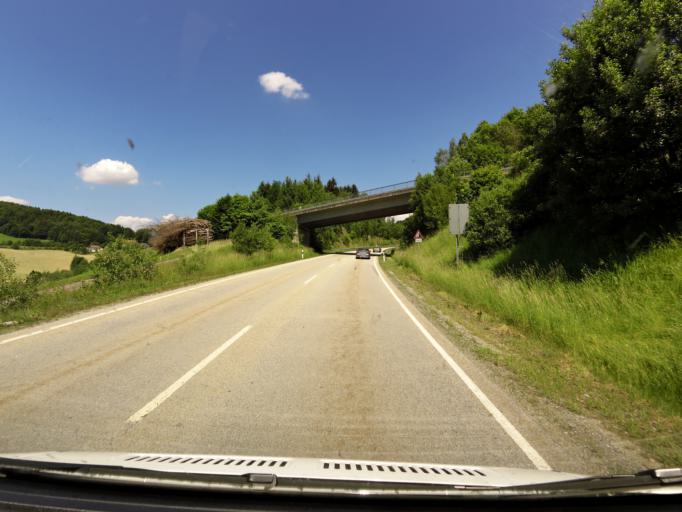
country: DE
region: Bavaria
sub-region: Lower Bavaria
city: Roehrnbach
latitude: 48.7791
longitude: 13.5045
